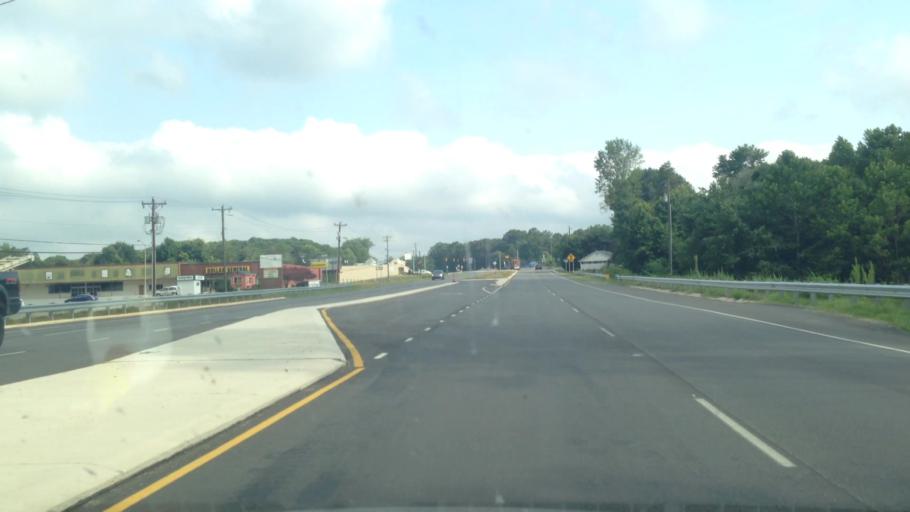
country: US
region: North Carolina
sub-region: Guilford County
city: Summerfield
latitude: 36.1900
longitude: -79.8904
